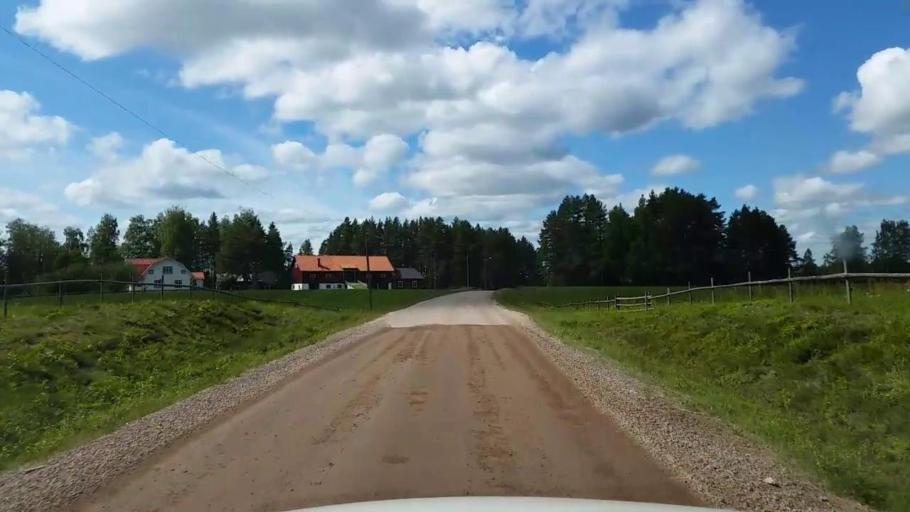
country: SE
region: Gaevleborg
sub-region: Ovanakers Kommun
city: Alfta
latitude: 61.4783
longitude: 15.9992
